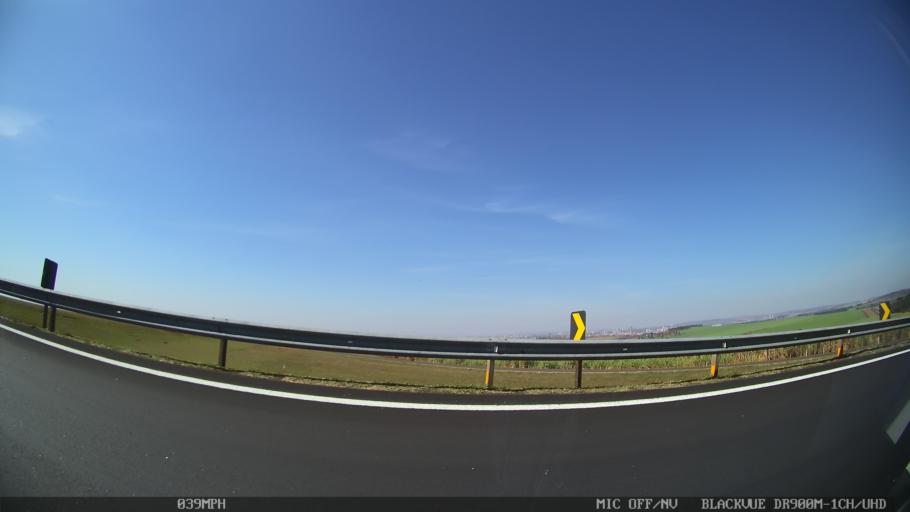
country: BR
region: Sao Paulo
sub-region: Ribeirao Preto
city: Ribeirao Preto
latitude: -21.1672
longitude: -47.8988
